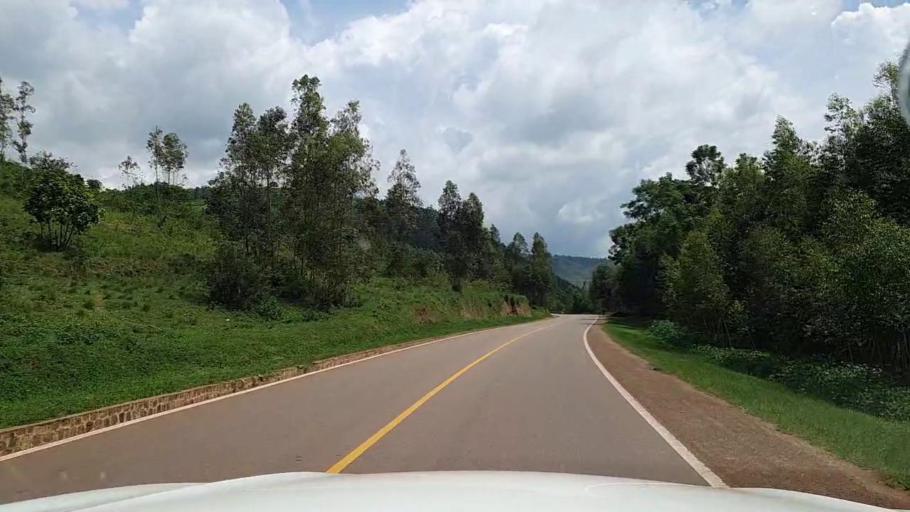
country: RW
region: Kigali
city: Kigali
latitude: -1.8242
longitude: 30.0808
